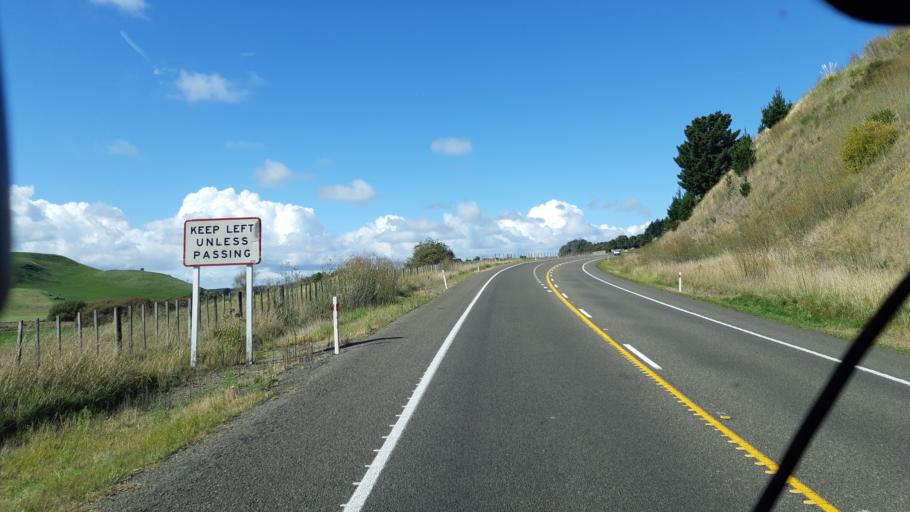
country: NZ
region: Manawatu-Wanganui
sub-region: Wanganui District
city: Wanganui
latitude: -39.9694
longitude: 175.1067
